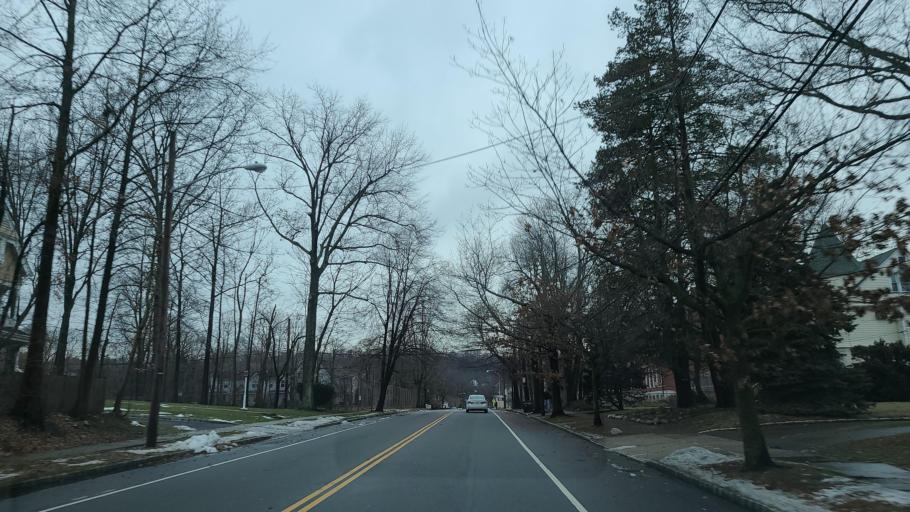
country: US
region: New Jersey
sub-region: Essex County
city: Upper Montclair
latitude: 40.8400
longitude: -74.2019
